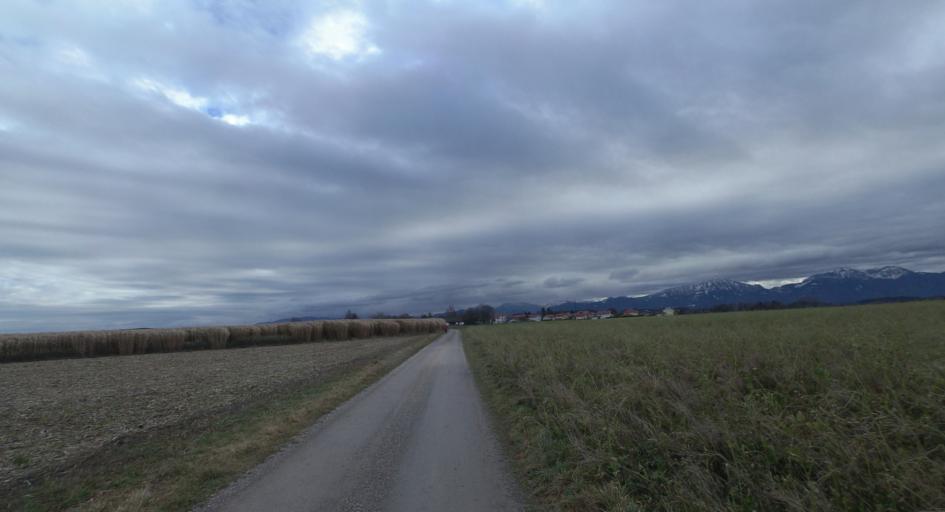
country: DE
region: Bavaria
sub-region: Upper Bavaria
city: Chieming
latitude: 47.9023
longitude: 12.5320
